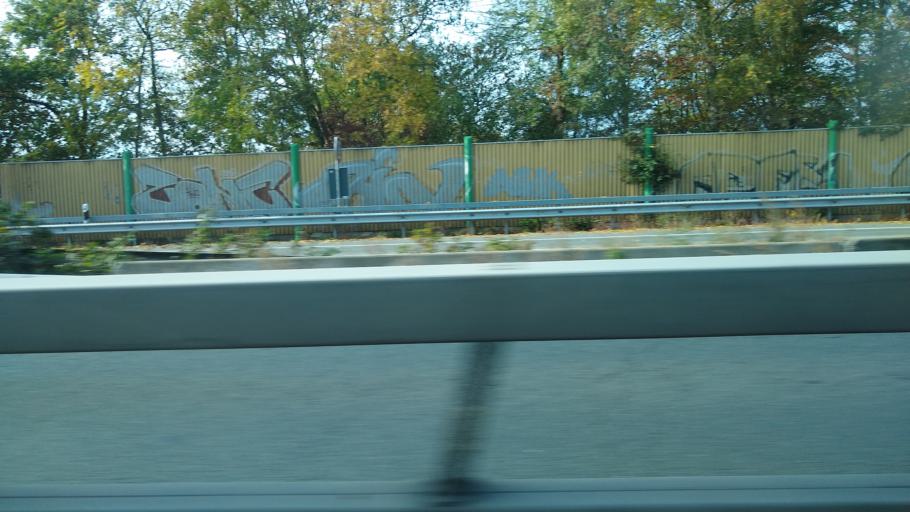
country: DE
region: Lower Saxony
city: Oldenburg
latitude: 53.1708
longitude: 8.2230
